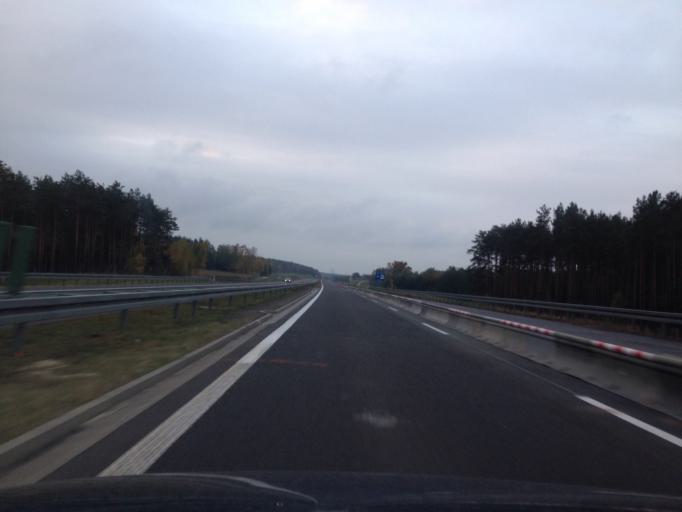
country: PL
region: Kujawsko-Pomorskie
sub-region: Powiat swiecki
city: Warlubie
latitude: 53.6545
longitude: 18.6387
